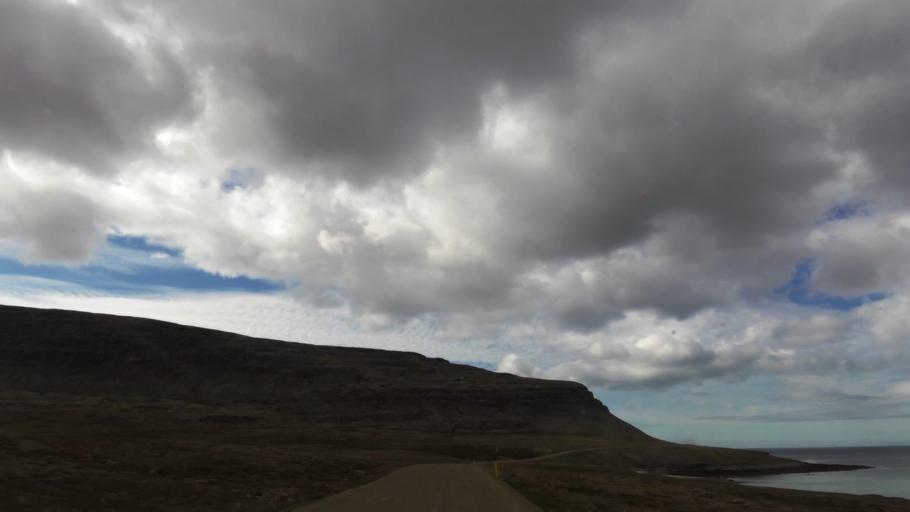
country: IS
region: West
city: Olafsvik
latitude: 65.5692
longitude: -24.0554
